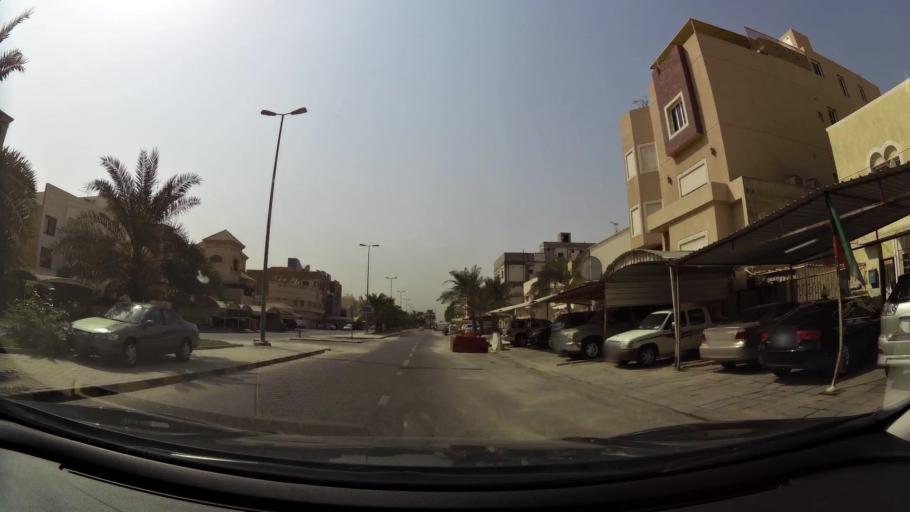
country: KW
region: Al Asimah
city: Ad Dasmah
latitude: 29.3507
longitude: 48.0080
